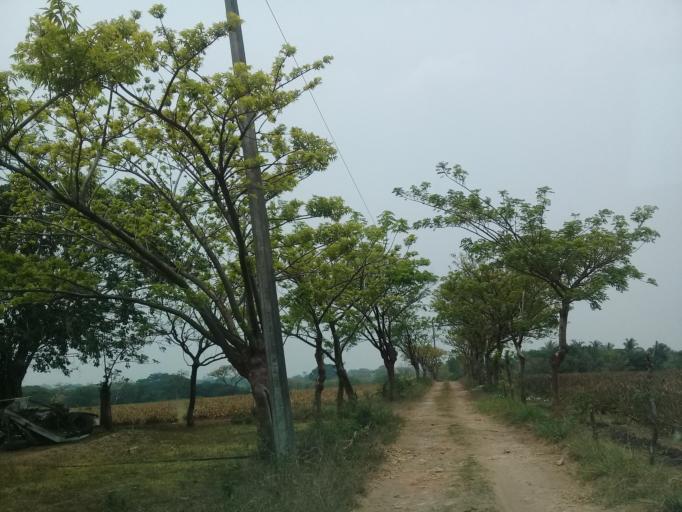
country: MX
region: Veracruz
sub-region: Medellin
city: La Laguna y Monte del Castillo
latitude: 18.9737
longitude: -96.1374
